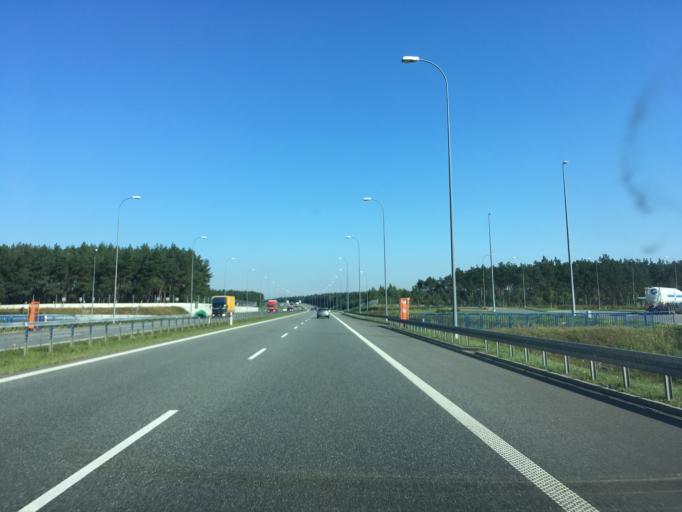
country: PL
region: Kujawsko-Pomorskie
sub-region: Powiat torunski
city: Lubicz Dolny
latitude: 53.1422
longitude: 18.7424
